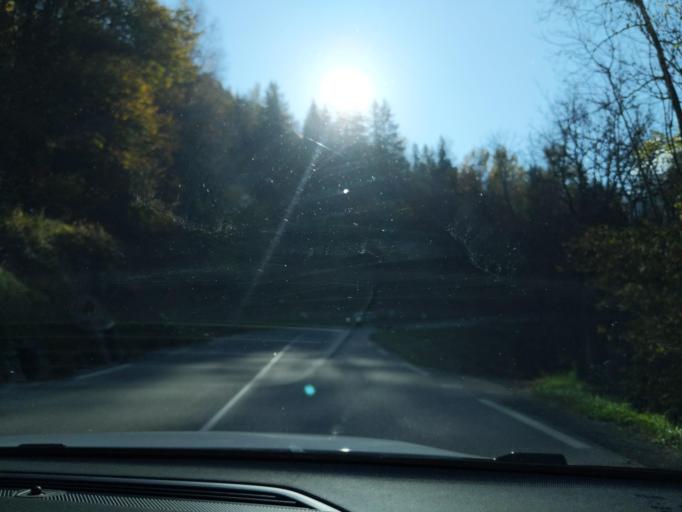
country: FR
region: Rhone-Alpes
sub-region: Departement de la Savoie
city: Seez
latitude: 45.5961
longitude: 6.8807
